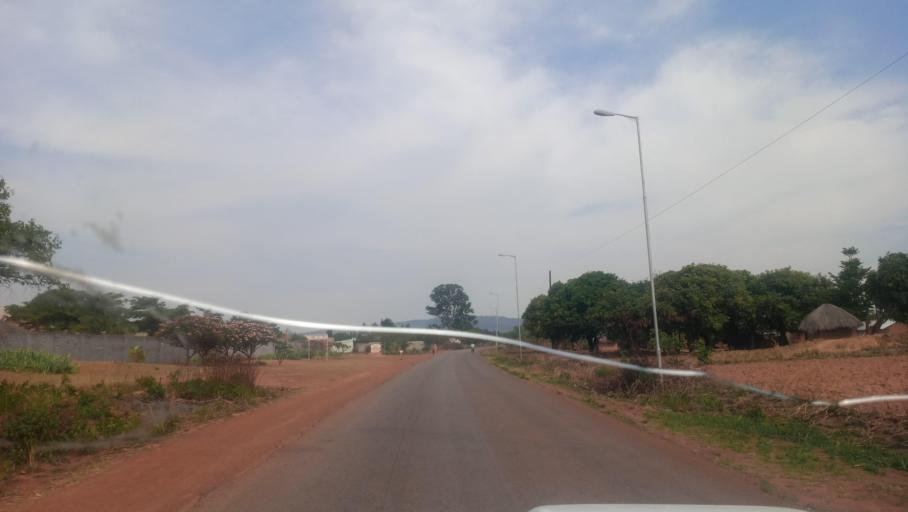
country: ZM
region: Northern
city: Mpika
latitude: -11.8331
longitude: 31.4220
